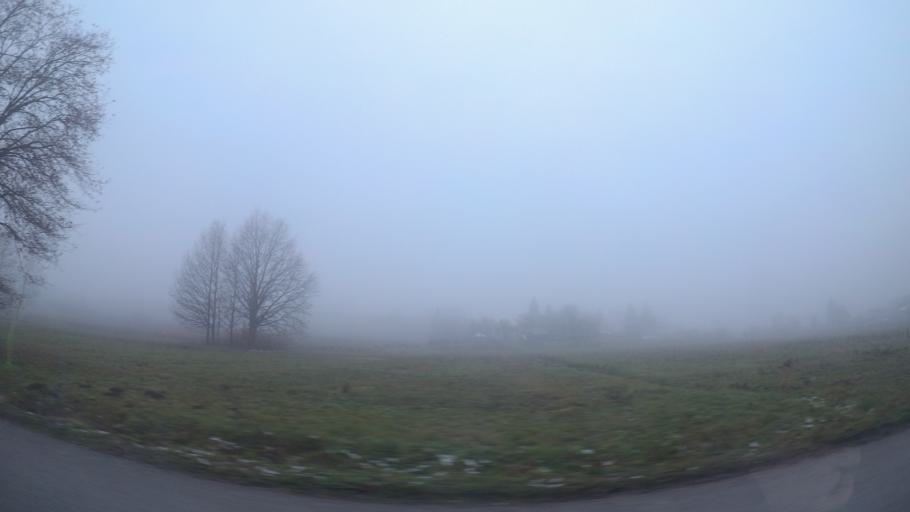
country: HR
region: Sisacko-Moslavacka
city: Glina
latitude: 45.3292
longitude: 16.0398
